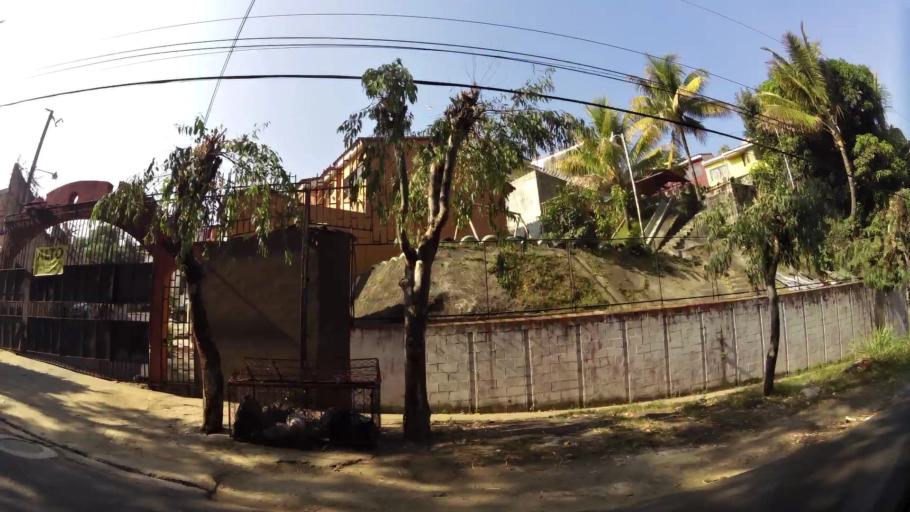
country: SV
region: La Libertad
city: Antiguo Cuscatlan
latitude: 13.6694
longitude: -89.2243
